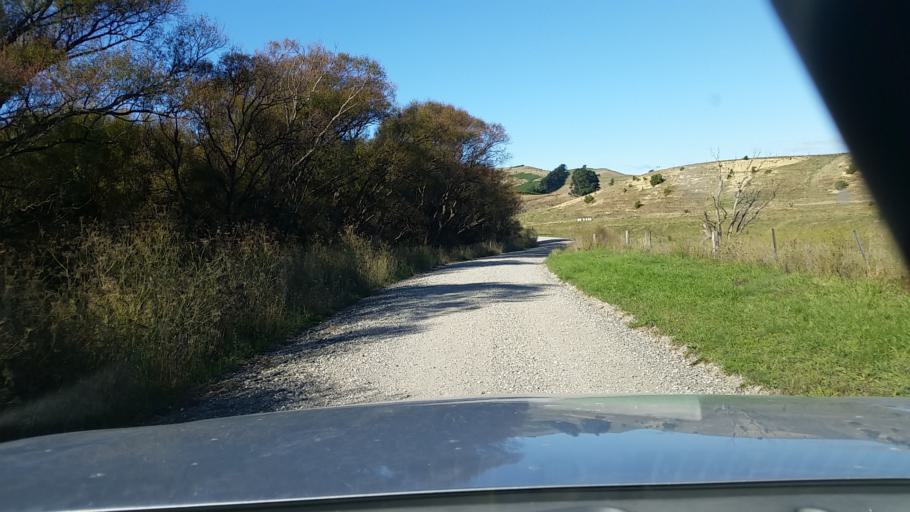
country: NZ
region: Marlborough
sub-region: Marlborough District
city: Blenheim
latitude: -41.6783
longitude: 174.1384
